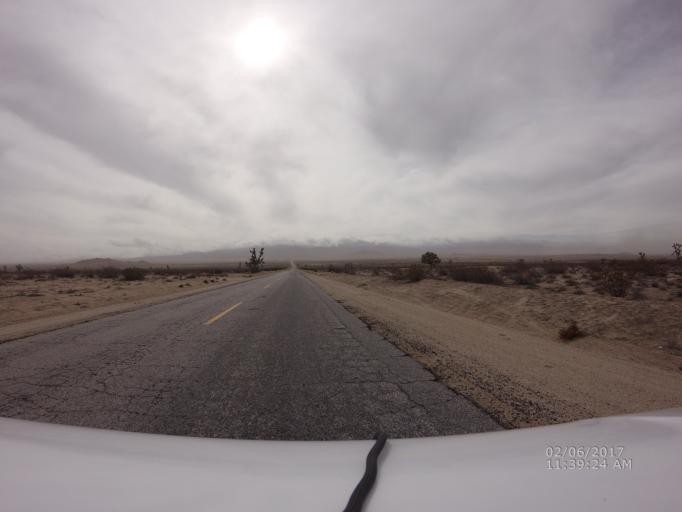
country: US
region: California
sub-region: Los Angeles County
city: Lake Los Angeles
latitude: 34.6243
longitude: -117.7027
